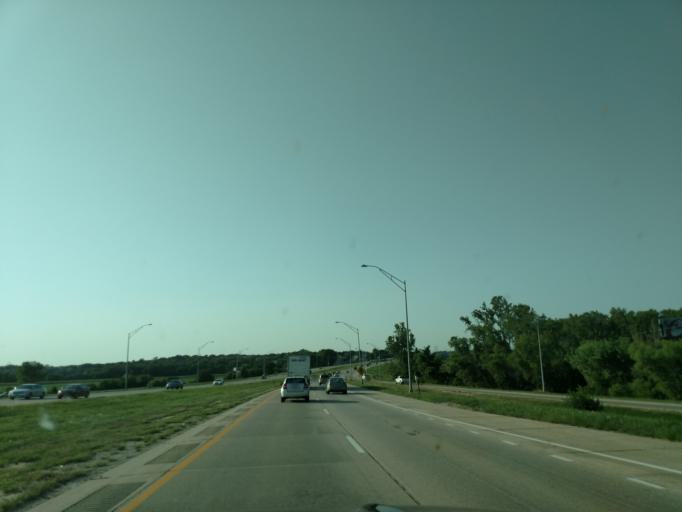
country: US
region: Nebraska
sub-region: Sarpy County
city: Offutt Air Force Base
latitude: 41.1418
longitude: -95.9375
